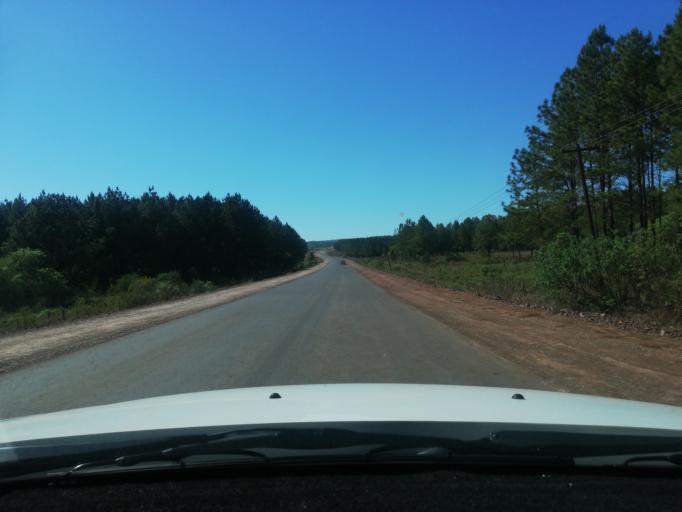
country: AR
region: Misiones
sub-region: Departamento de Candelaria
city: Candelaria
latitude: -27.5234
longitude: -55.7241
